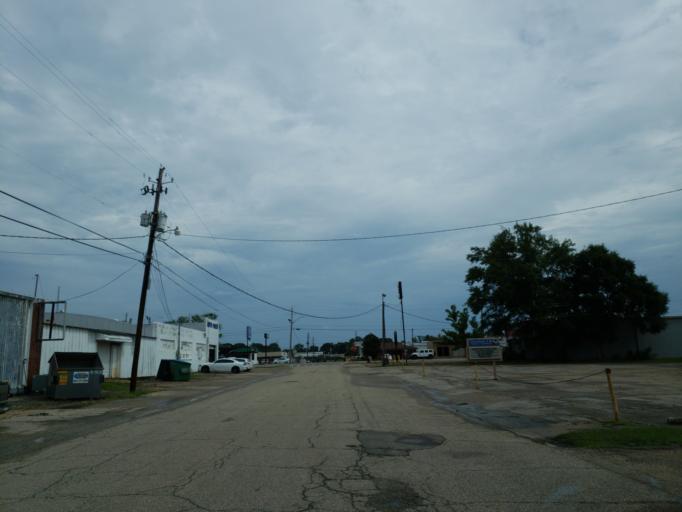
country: US
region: Mississippi
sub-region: Forrest County
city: Hattiesburg
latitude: 31.3154
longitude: -89.3089
